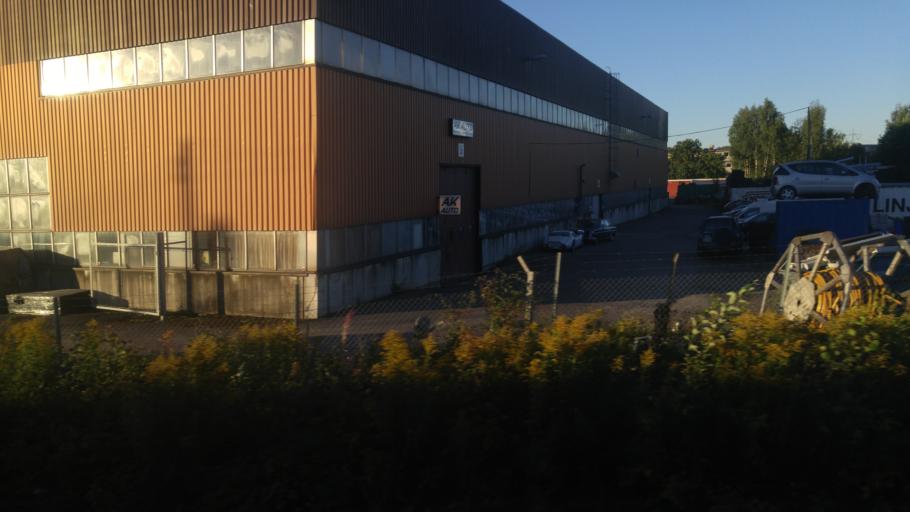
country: NO
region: Akershus
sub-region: Lorenskog
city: Kjenn
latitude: 59.9538
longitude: 10.8975
